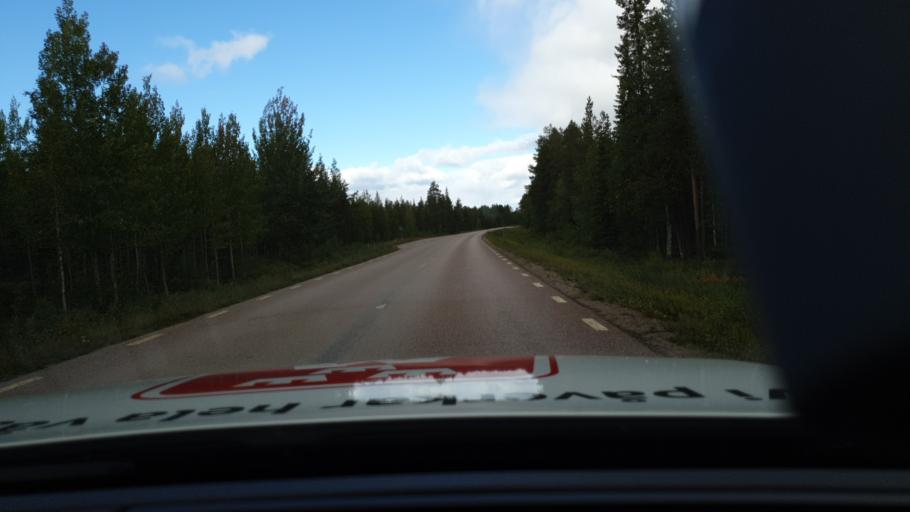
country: SE
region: Norrbotten
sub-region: Pajala Kommun
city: Pajala
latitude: 67.2328
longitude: 22.7814
